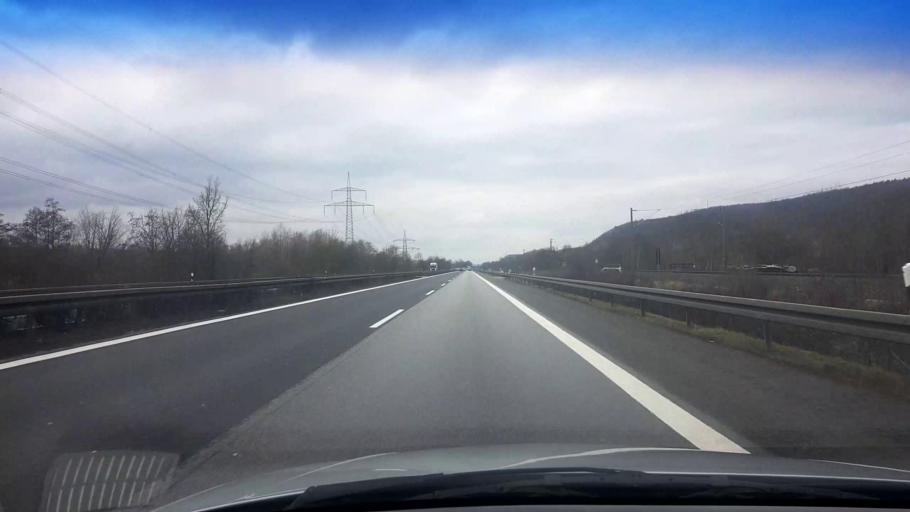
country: DE
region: Bavaria
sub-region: Regierungsbezirk Unterfranken
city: Stettfeld
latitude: 49.9725
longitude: 10.7009
